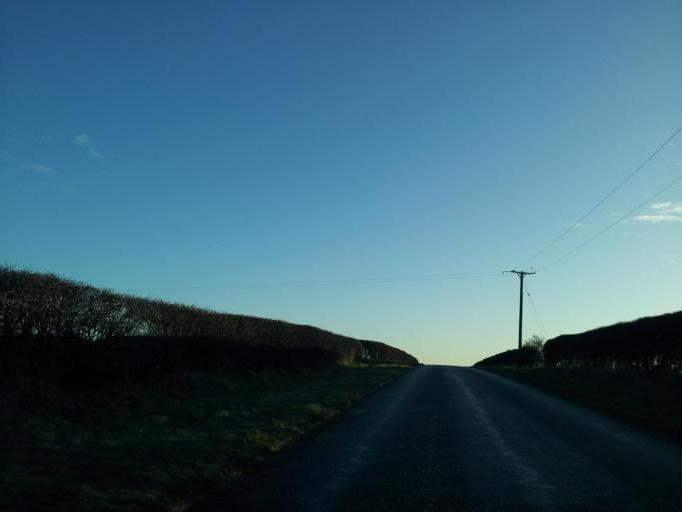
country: GB
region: England
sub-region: Lincolnshire
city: Horncastle
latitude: 53.2600
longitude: -0.0864
